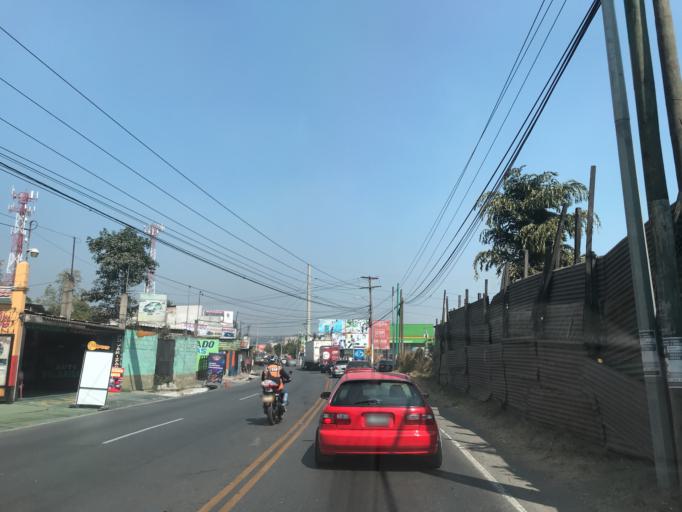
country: GT
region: Guatemala
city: Petapa
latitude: 14.5150
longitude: -90.5641
